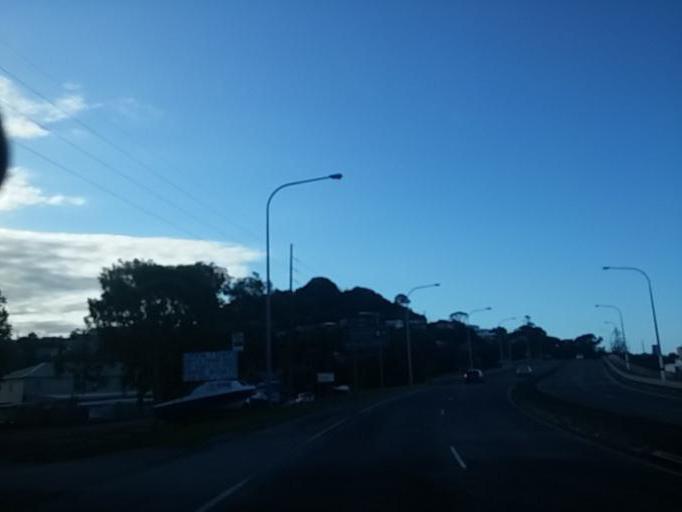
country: AU
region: New South Wales
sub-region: Tweed
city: Tweed Heads West
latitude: -28.1853
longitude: 153.5382
